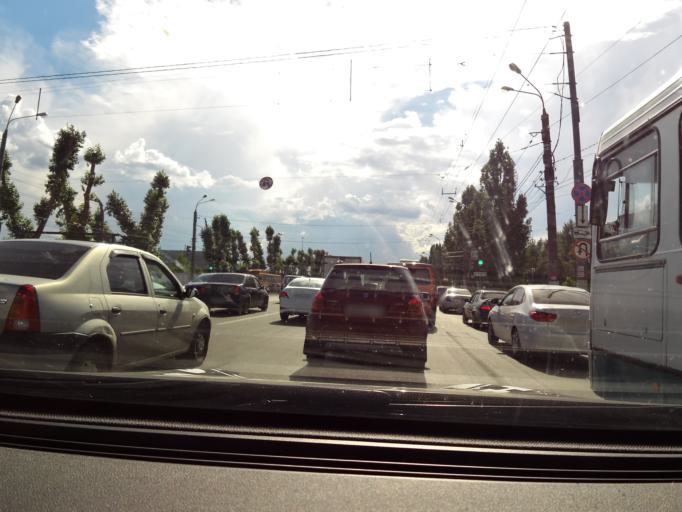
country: RU
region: Nizjnij Novgorod
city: Nizhniy Novgorod
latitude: 56.3217
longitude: 43.9403
